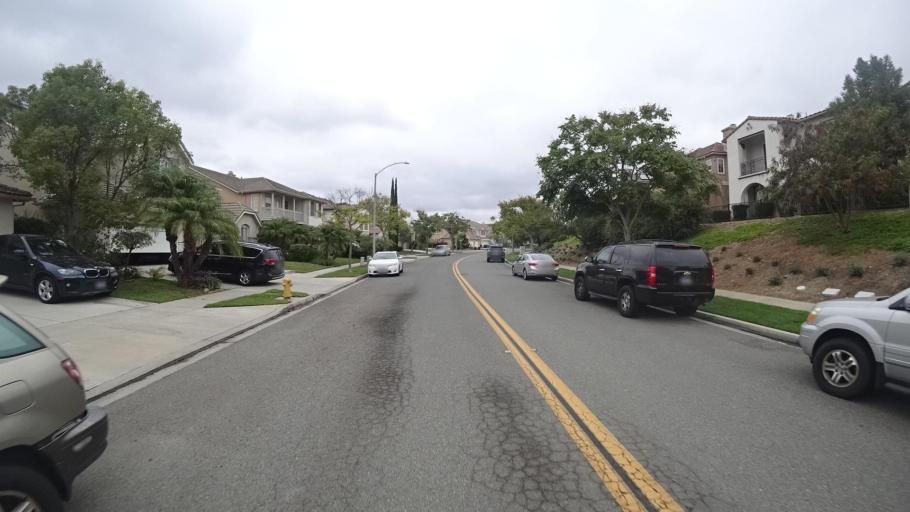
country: US
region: California
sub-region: San Diego County
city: Fairbanks Ranch
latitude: 33.0159
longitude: -117.1192
